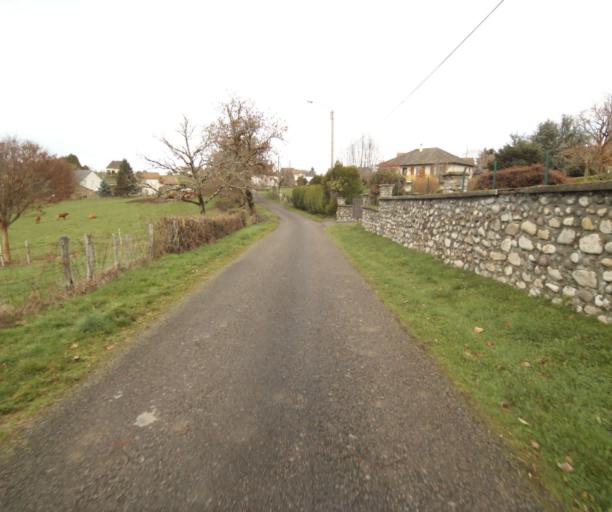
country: FR
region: Limousin
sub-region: Departement de la Correze
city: Chameyrat
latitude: 45.2634
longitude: 1.7227
